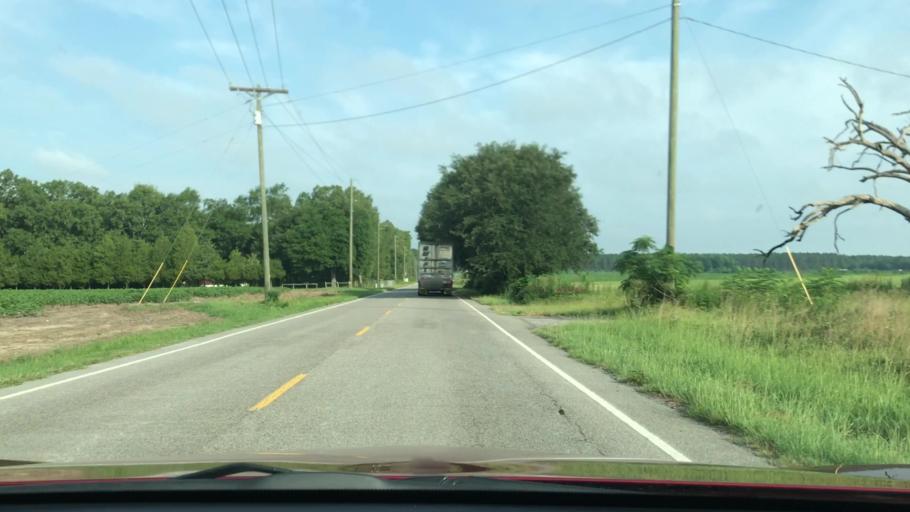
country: US
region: South Carolina
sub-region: Barnwell County
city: Blackville
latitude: 33.6093
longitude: -81.2733
